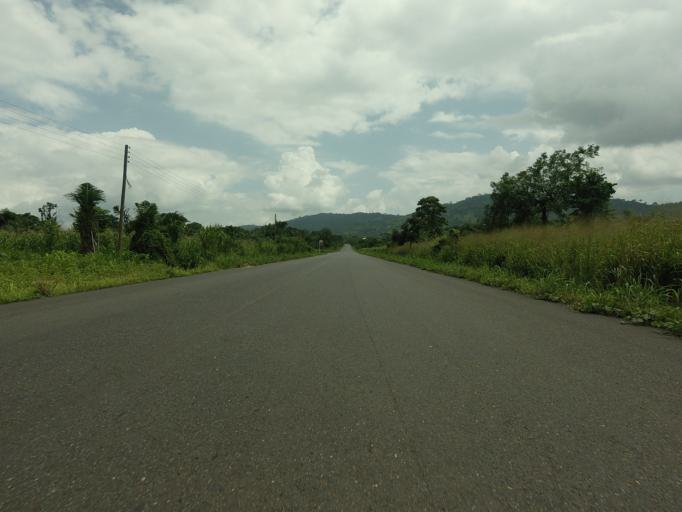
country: GH
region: Volta
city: Ho
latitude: 6.5414
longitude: 0.2436
